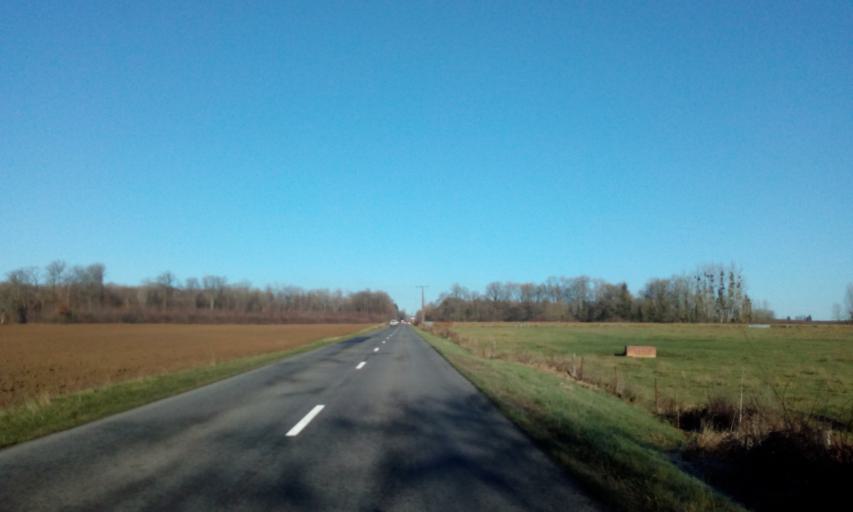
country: FR
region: Champagne-Ardenne
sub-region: Departement des Ardennes
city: Rimogne
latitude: 49.8165
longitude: 4.5095
